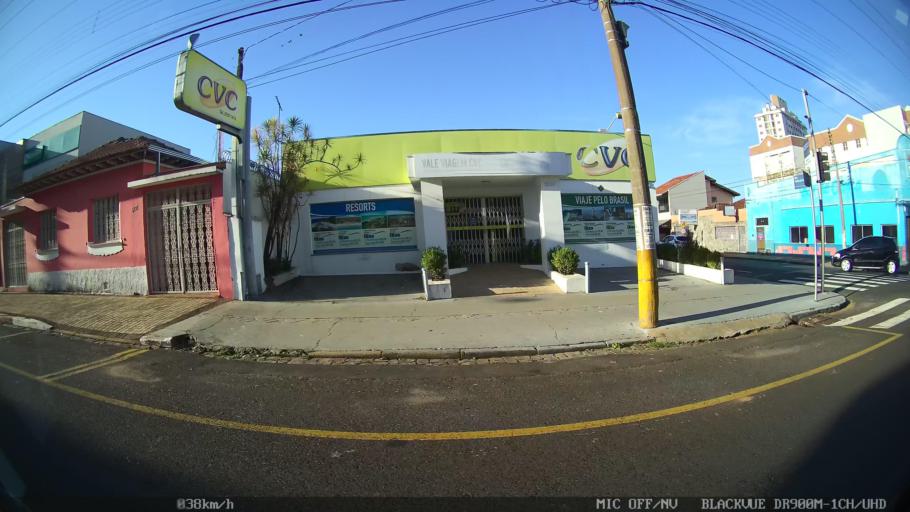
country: BR
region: Sao Paulo
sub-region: Franca
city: Franca
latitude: -20.5342
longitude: -47.3947
